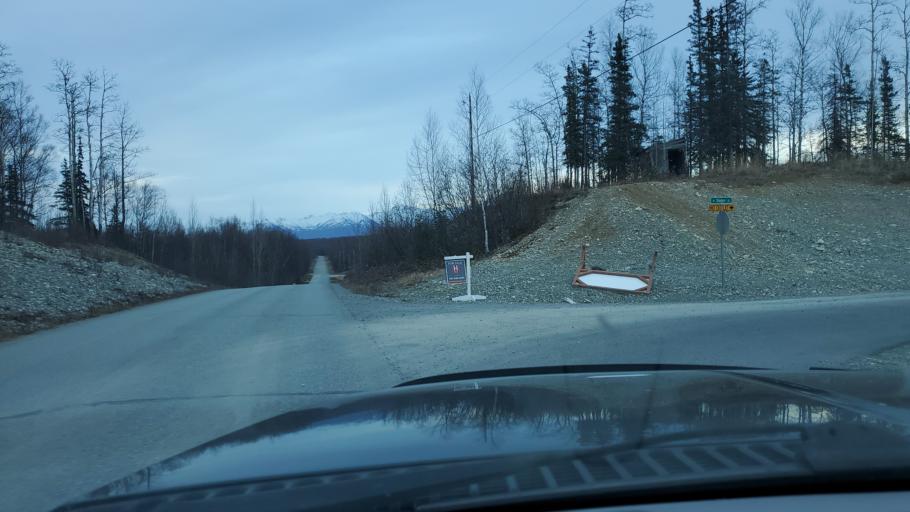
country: US
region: Alaska
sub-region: Matanuska-Susitna Borough
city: Lakes
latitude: 61.6572
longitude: -149.2906
